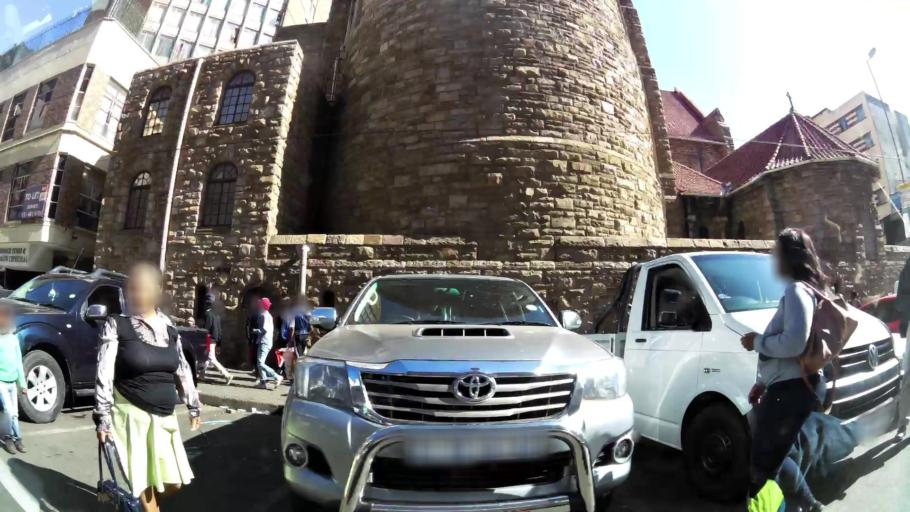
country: ZA
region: Gauteng
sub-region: City of Johannesburg Metropolitan Municipality
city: Johannesburg
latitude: -26.1993
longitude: 28.0449
